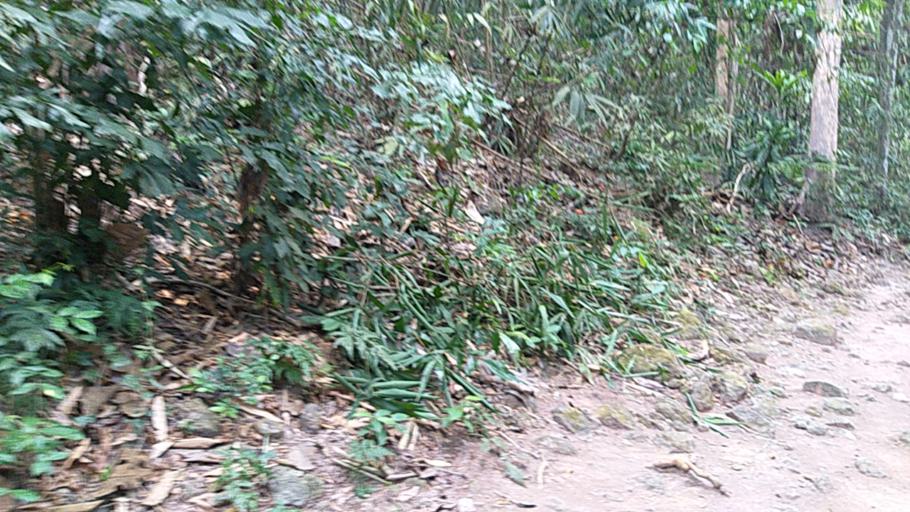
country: TH
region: Sara Buri
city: Wihan Daeng
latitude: 14.4361
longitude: 100.9629
